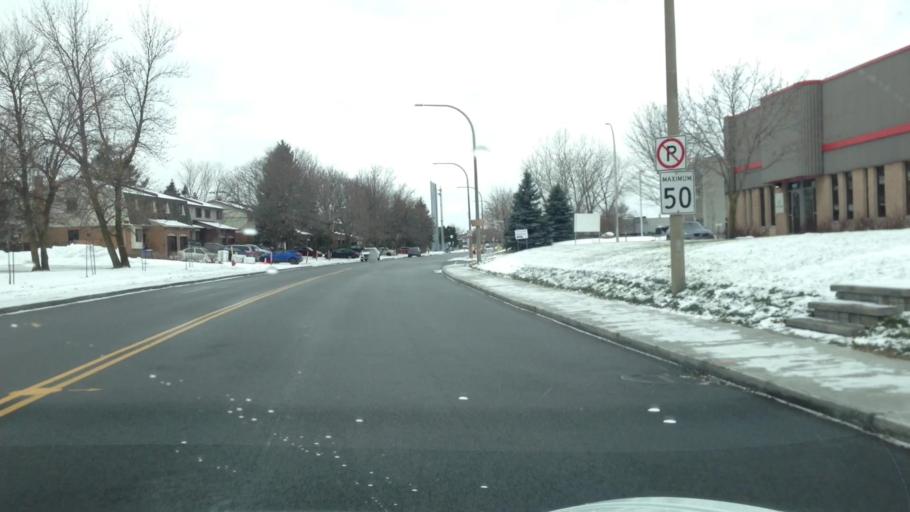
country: CA
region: Quebec
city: Kirkland
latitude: 45.4501
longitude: -73.8433
